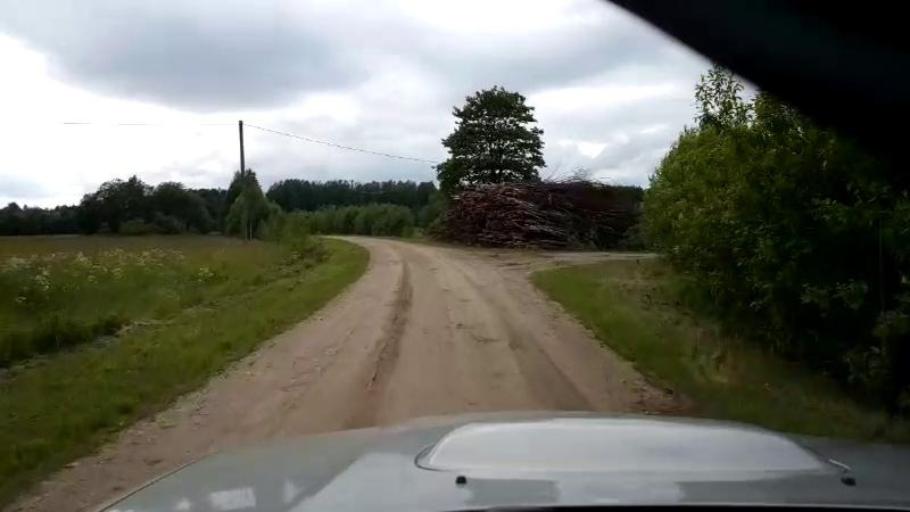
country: EE
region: Paernumaa
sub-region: Halinga vald
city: Parnu-Jaagupi
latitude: 58.5638
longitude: 24.5712
